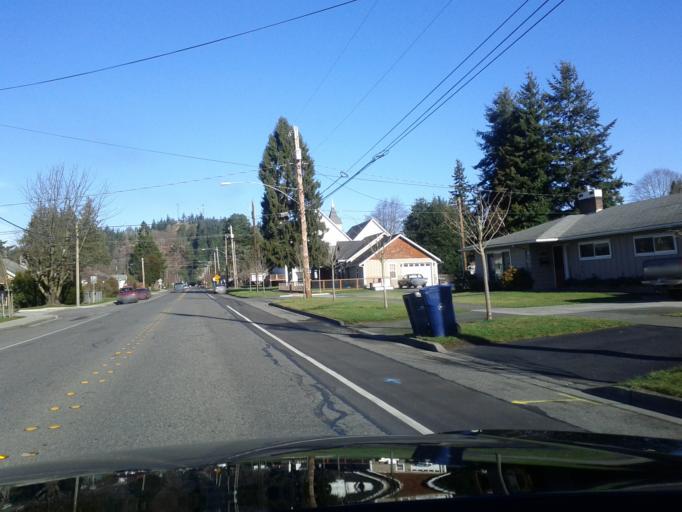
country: US
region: Washington
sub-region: Skagit County
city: Burlington
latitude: 48.4704
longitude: -122.3248
